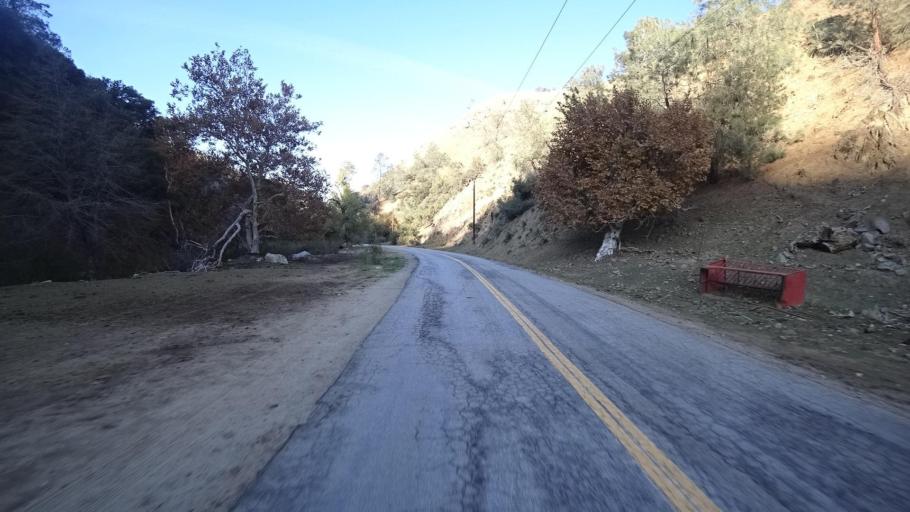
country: US
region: California
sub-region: Kern County
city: Golden Hills
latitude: 35.3152
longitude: -118.5149
